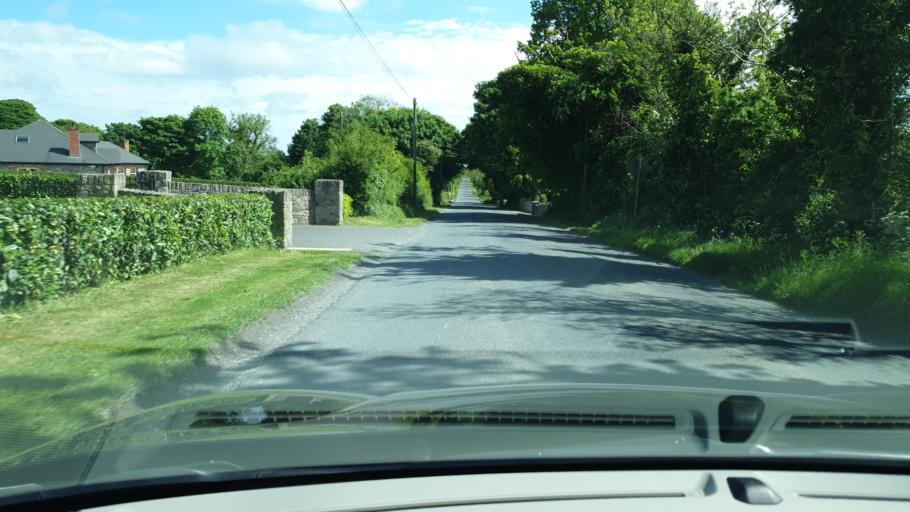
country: IE
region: Leinster
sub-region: An Mhi
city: Slane
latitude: 53.7599
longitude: -6.6089
